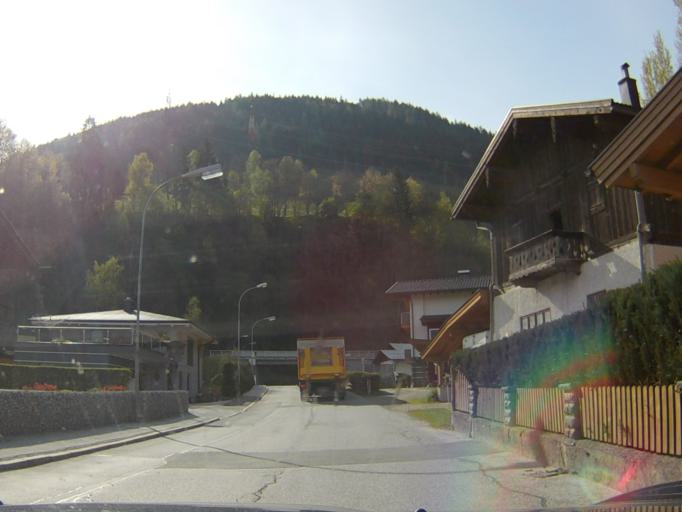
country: AT
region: Salzburg
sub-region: Politischer Bezirk Zell am See
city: Mittersill
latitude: 47.2741
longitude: 12.4844
